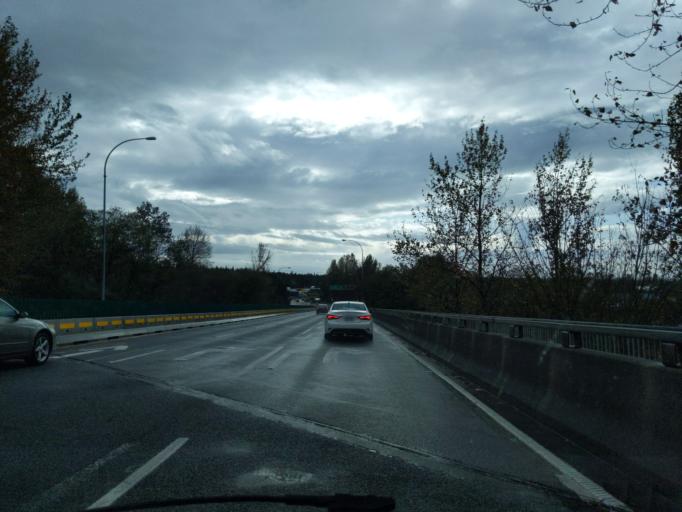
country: CA
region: British Columbia
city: Delta
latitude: 49.1508
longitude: -122.9350
